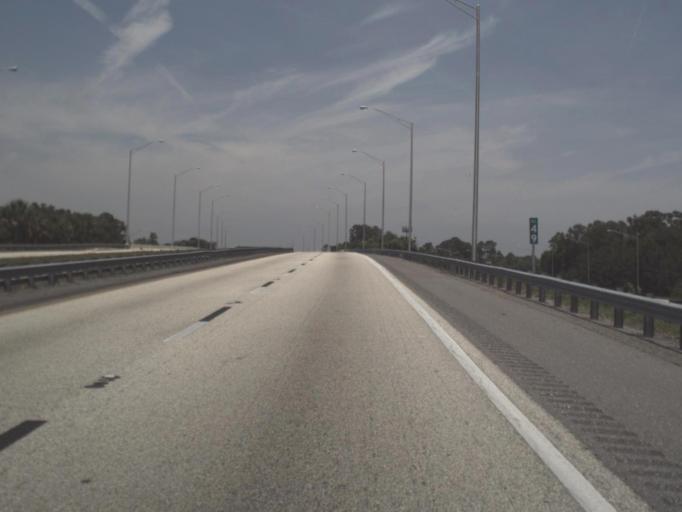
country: US
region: Florida
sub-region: Duval County
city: Atlantic Beach
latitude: 30.3142
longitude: -81.5241
